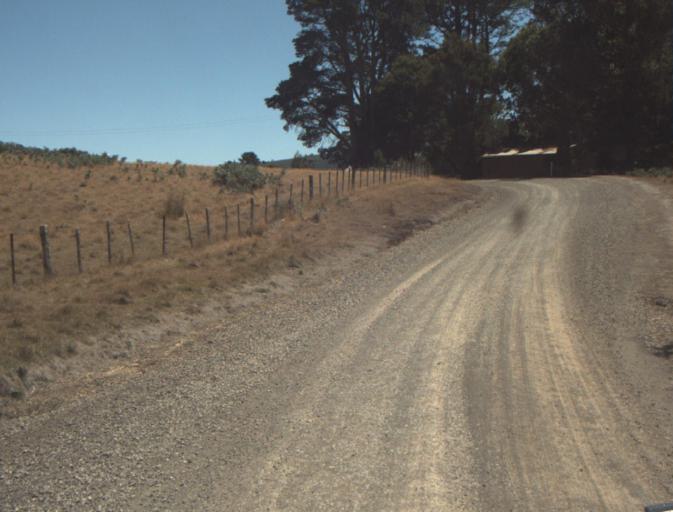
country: AU
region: Tasmania
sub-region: Dorset
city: Scottsdale
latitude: -41.2976
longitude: 147.3561
